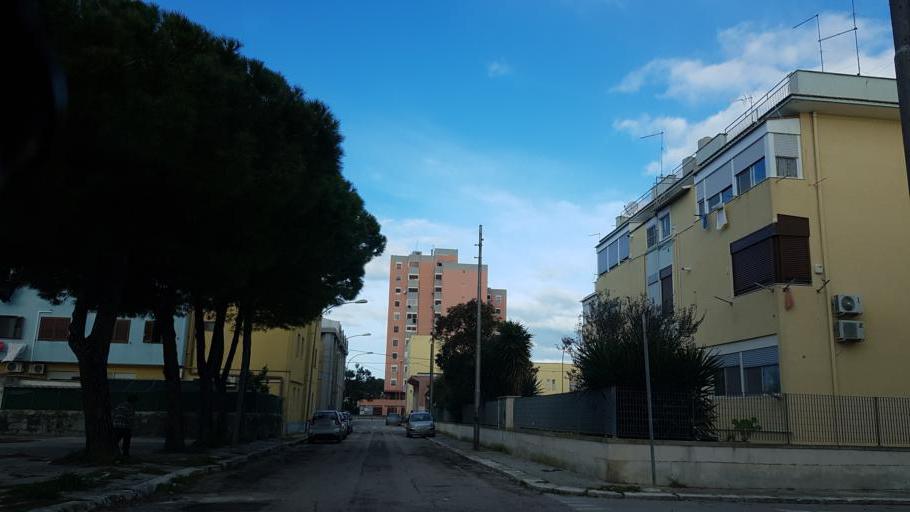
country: IT
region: Apulia
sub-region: Provincia di Brindisi
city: Brindisi
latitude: 40.6311
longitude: 17.9539
